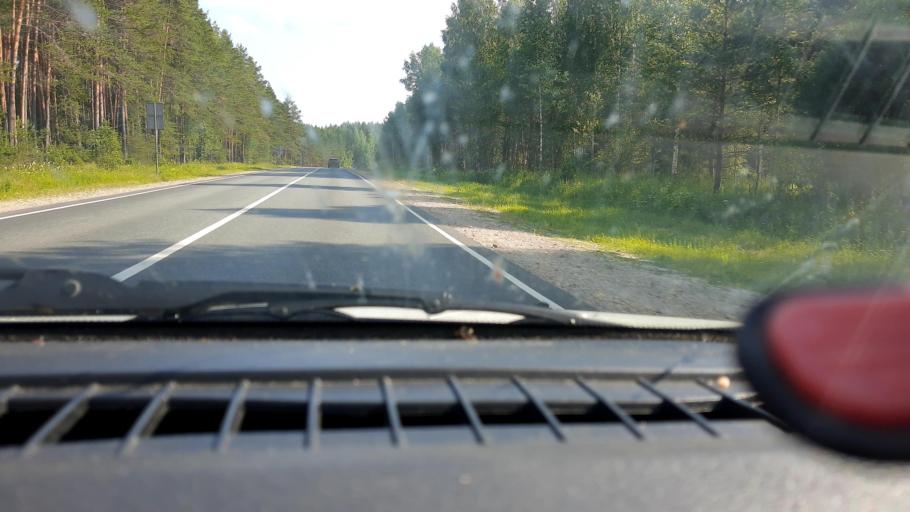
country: RU
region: Nizjnij Novgorod
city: Krasnyye Baki
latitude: 57.0243
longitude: 45.1166
